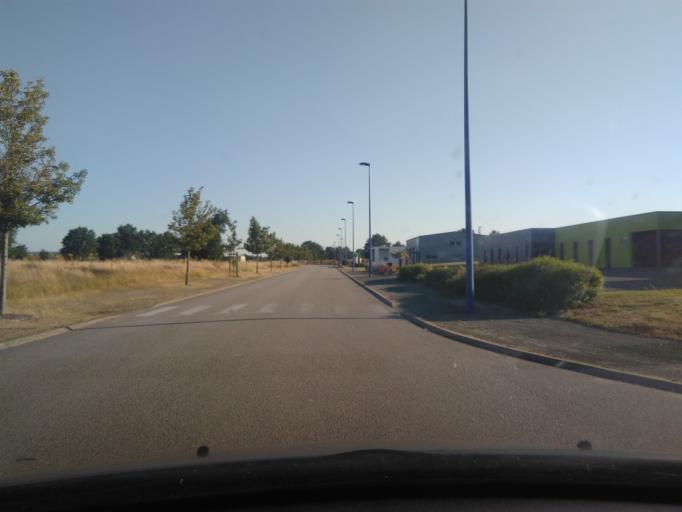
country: FR
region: Pays de la Loire
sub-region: Departement de la Vendee
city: Mouilleron-le-Captif
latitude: 46.7395
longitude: -1.4266
